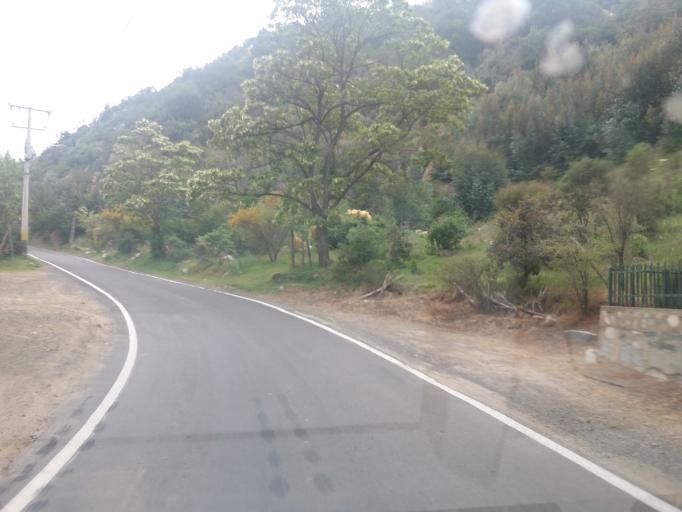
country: CL
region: Valparaiso
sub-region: Provincia de Marga Marga
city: Limache
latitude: -33.0330
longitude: -71.0852
